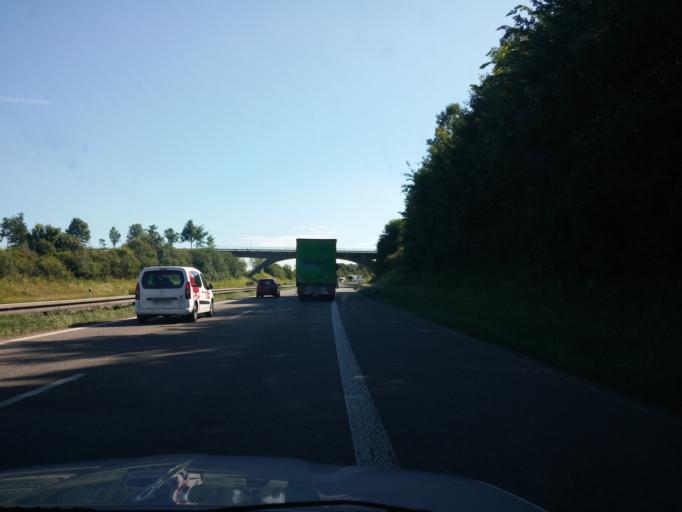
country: DE
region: Baden-Wuerttemberg
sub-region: Tuebingen Region
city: Leutkirch im Allgau
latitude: 47.8588
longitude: 10.0056
